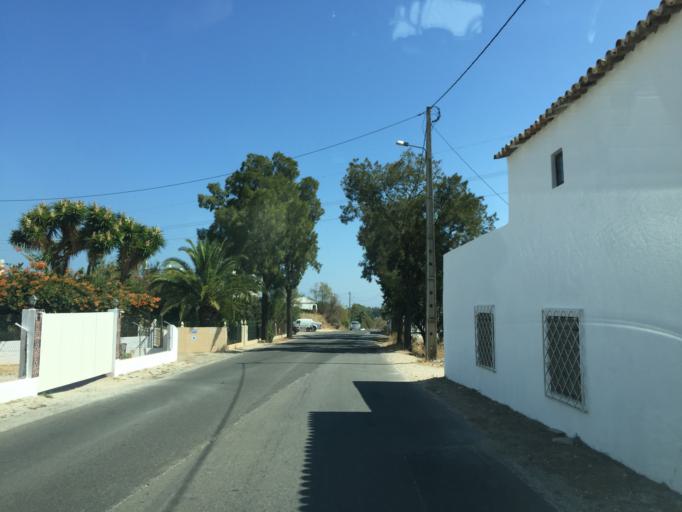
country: PT
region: Faro
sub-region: Olhao
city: Olhao
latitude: 37.0475
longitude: -7.8639
